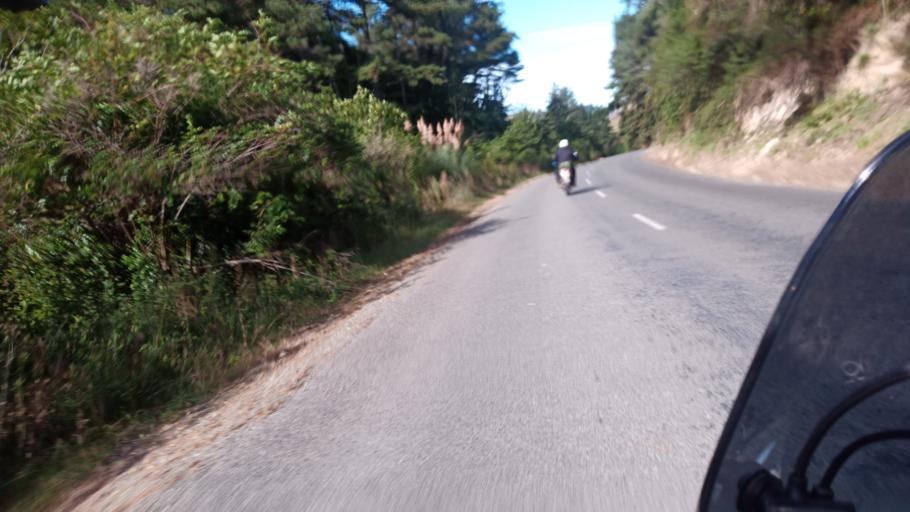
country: NZ
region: Hawke's Bay
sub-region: Wairoa District
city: Wairoa
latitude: -39.0372
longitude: 177.1055
